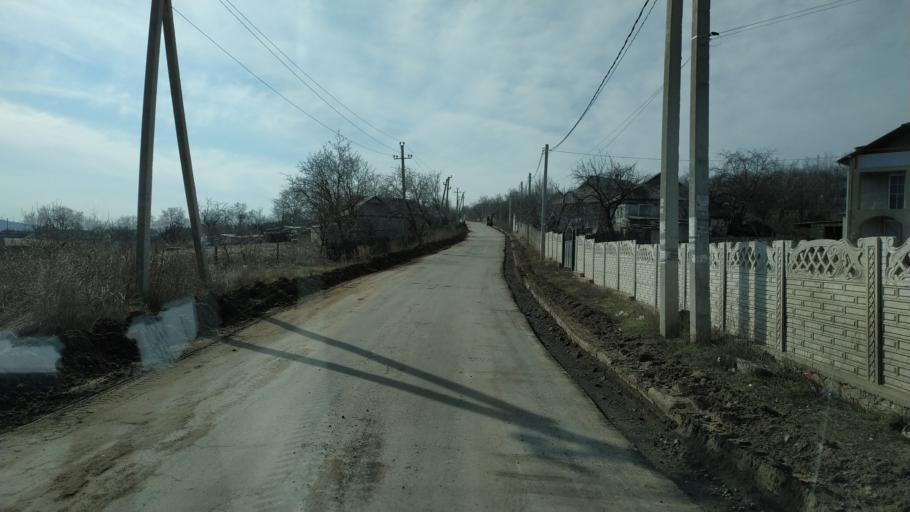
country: MD
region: Nisporeni
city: Nisporeni
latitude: 47.1564
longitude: 28.1329
